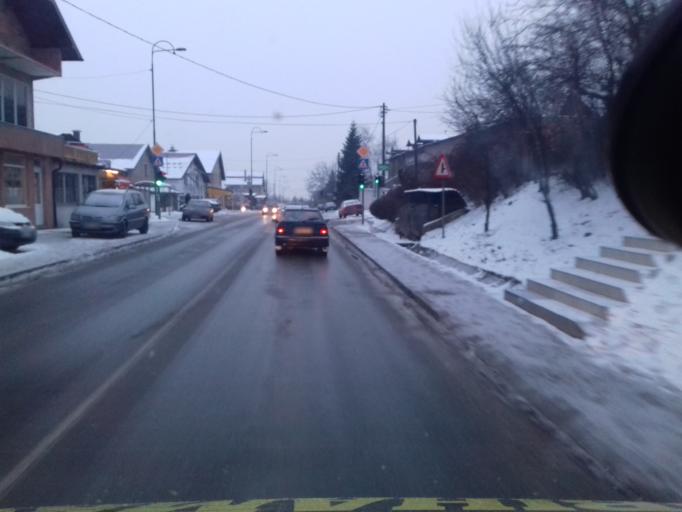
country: BA
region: Federation of Bosnia and Herzegovina
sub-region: Kanton Sarajevo
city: Sarajevo
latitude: 43.8525
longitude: 18.3599
